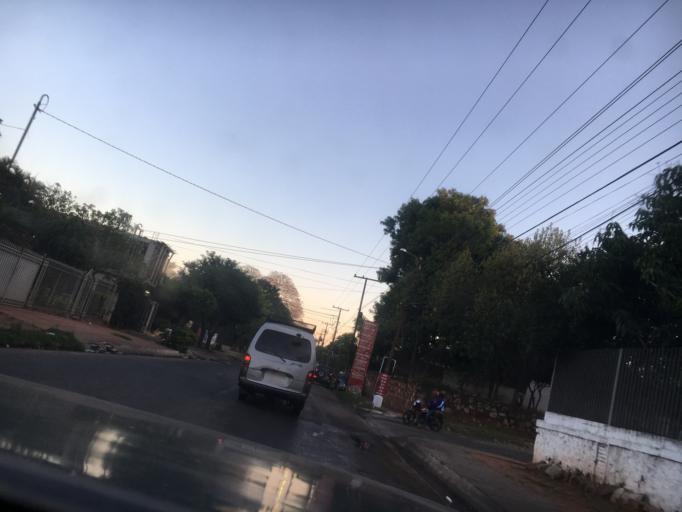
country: PY
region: Central
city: Lambare
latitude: -25.3484
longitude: -57.6010
